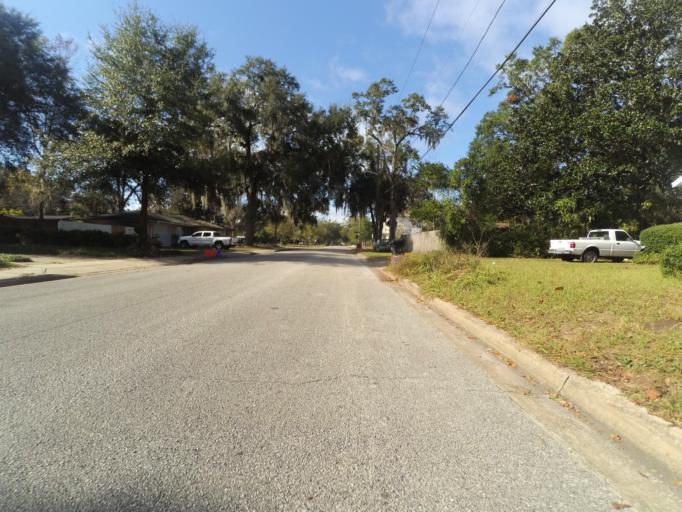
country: US
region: Florida
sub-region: Alachua County
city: Gainesville
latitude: 29.6649
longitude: -82.3280
